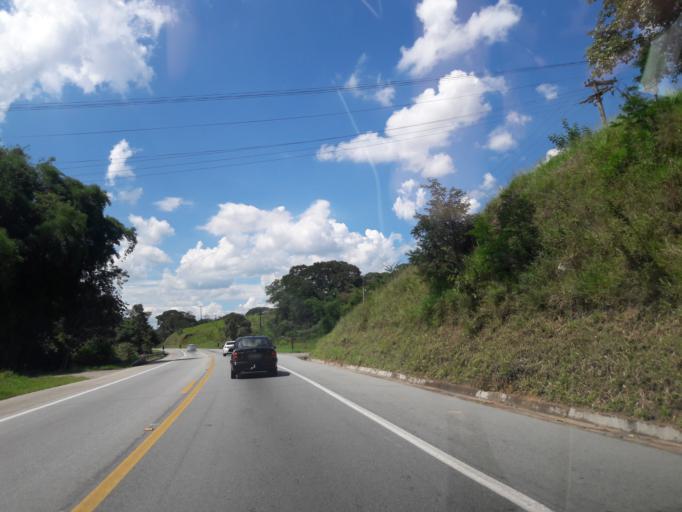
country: BR
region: Sao Paulo
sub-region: Francisco Morato
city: Francisco Morato
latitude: -23.3099
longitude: -46.8148
